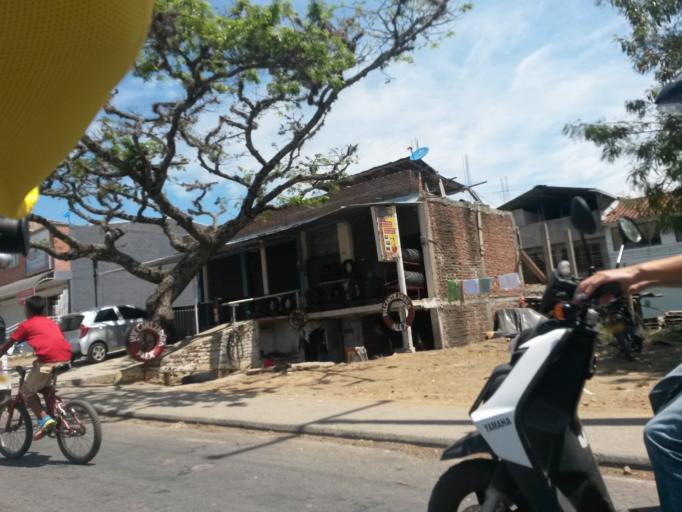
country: CO
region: Cauca
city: Santander de Quilichao
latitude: 3.0130
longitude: -76.4837
